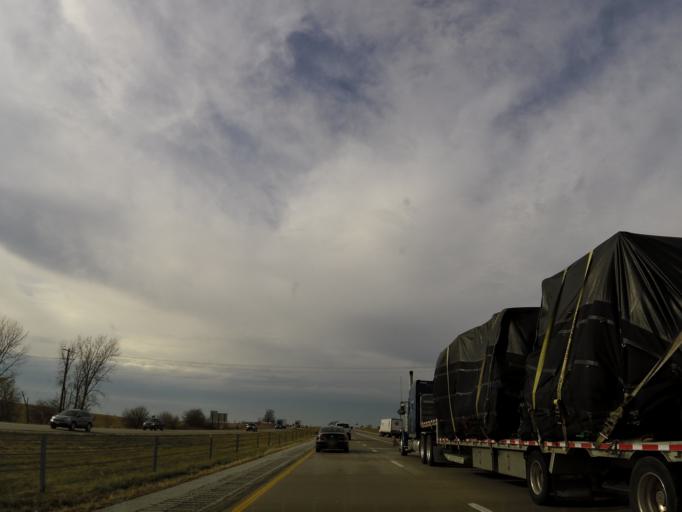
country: US
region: Iowa
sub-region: Scott County
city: Eldridge
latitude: 41.6001
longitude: -90.6233
